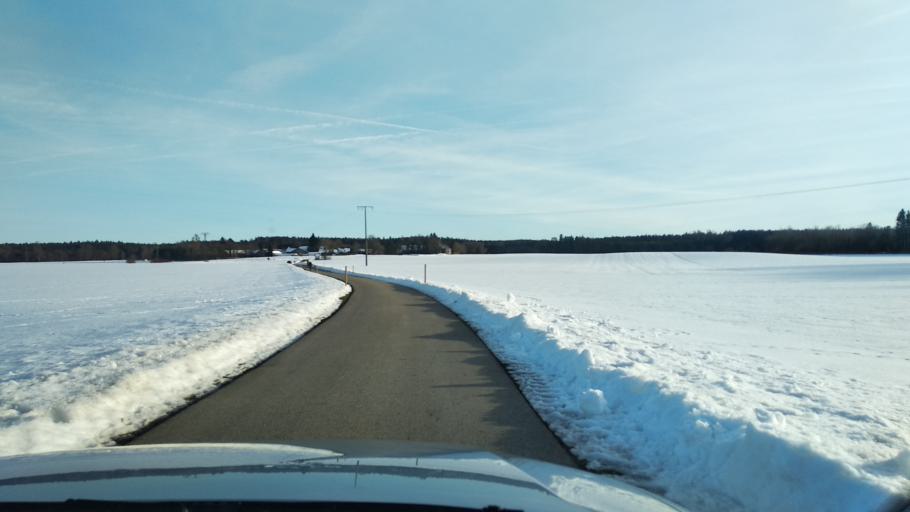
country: DE
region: Bavaria
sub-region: Upper Bavaria
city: Kirchseeon
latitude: 48.0753
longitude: 11.8640
